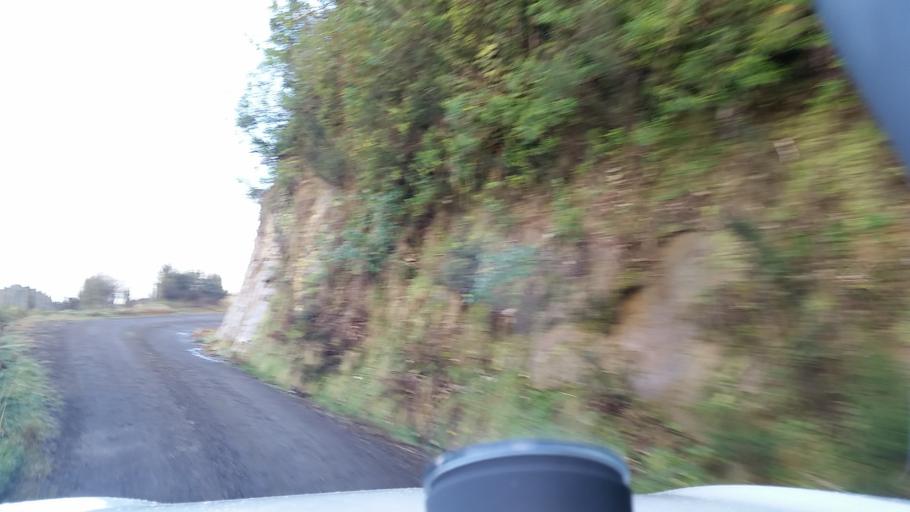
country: NZ
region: Taranaki
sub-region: South Taranaki District
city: Eltham
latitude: -39.4157
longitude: 174.5601
